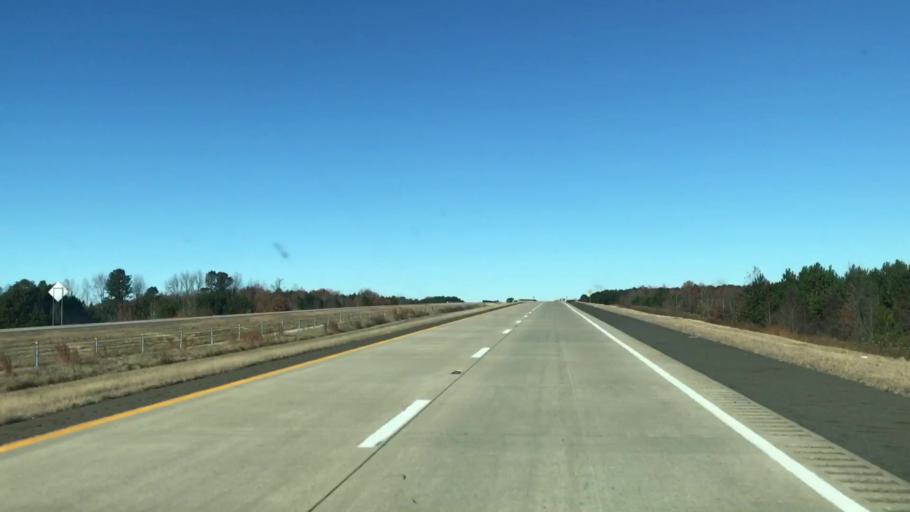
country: US
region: Texas
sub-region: Bowie County
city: Texarkana
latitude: 33.2482
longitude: -93.8829
